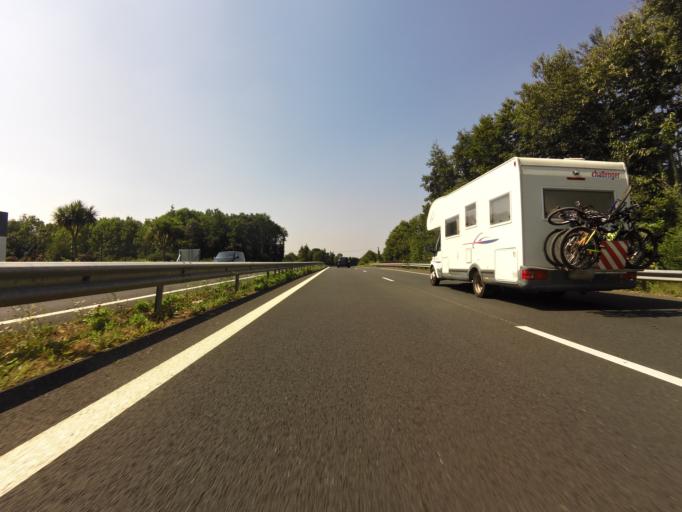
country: FR
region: Brittany
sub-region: Departement du Finistere
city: Plomelin
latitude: 47.9619
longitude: -4.1555
